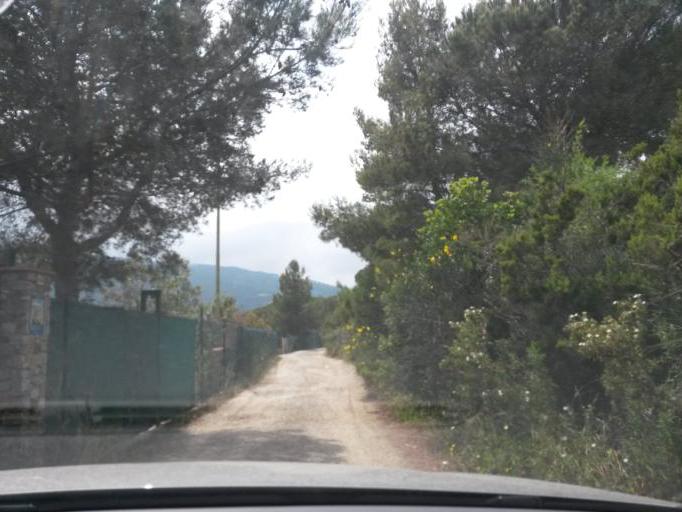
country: IT
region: Tuscany
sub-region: Provincia di Livorno
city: Porto Azzurro
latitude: 42.7511
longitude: 10.4085
